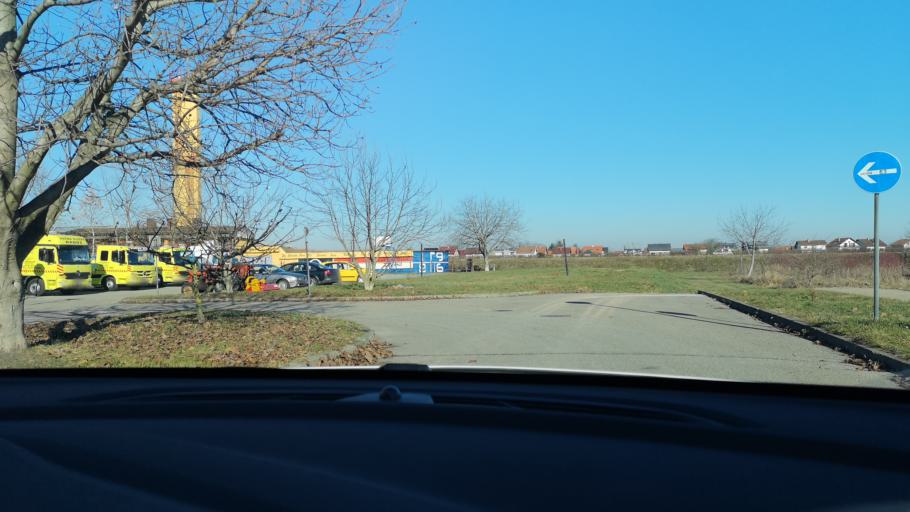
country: HR
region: Zagrebacka
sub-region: Grad Velika Gorica
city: Velika Gorica
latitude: 45.7232
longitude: 16.0656
